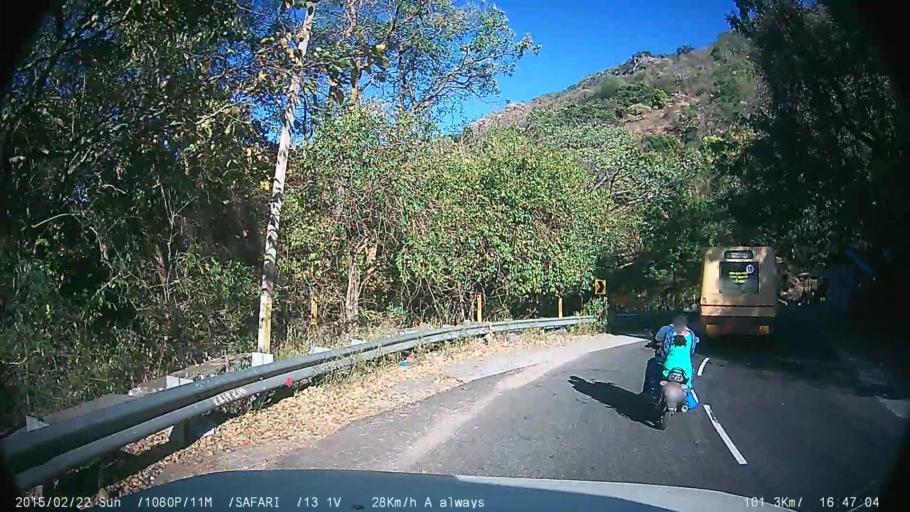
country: IN
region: Tamil Nadu
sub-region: Theni
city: Gudalur
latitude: 9.6217
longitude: 77.1924
